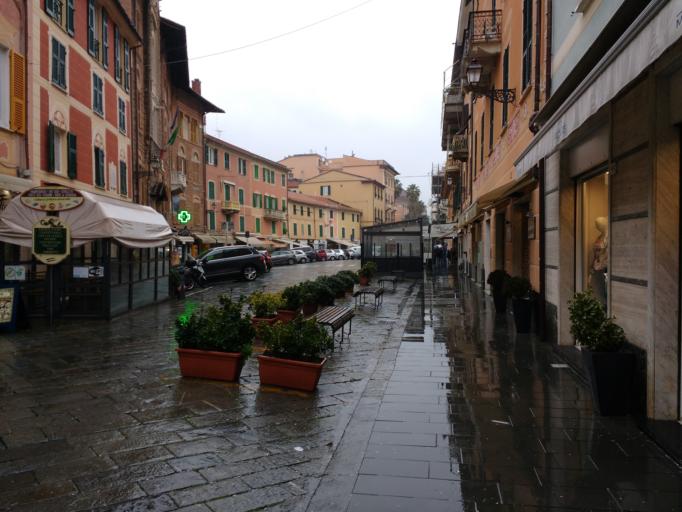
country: IT
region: Liguria
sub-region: Provincia di Genova
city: Sestri Levante
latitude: 44.2719
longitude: 9.3960
